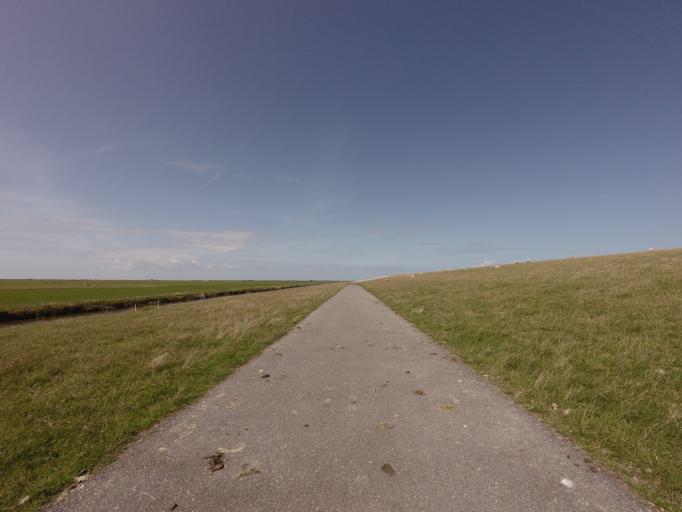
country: NL
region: Friesland
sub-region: Gemeente Dongeradeel
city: Holwerd
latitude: 53.3674
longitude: 5.8607
